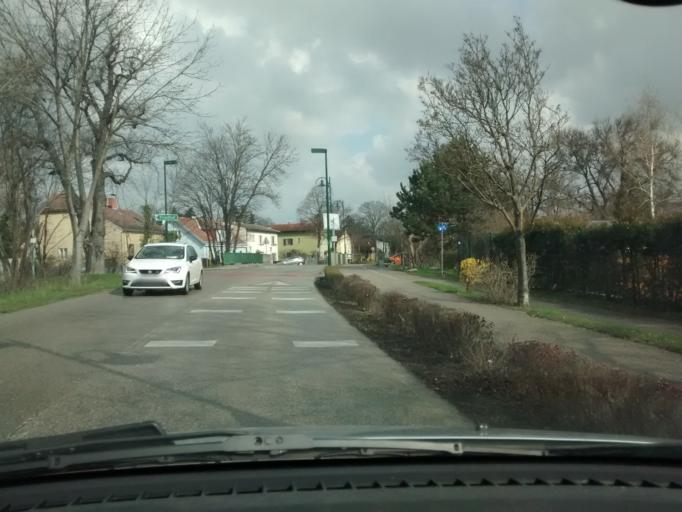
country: AT
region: Lower Austria
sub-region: Politischer Bezirk Modling
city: Biedermannsdorf
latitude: 48.0793
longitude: 16.3518
